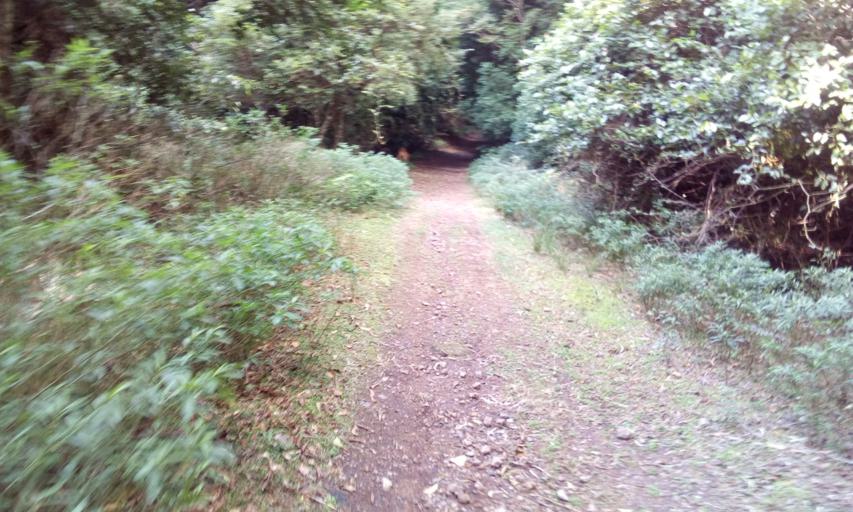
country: AU
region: New South Wales
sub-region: Wollongong
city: Cordeaux Heights
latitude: -34.4444
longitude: 150.8009
